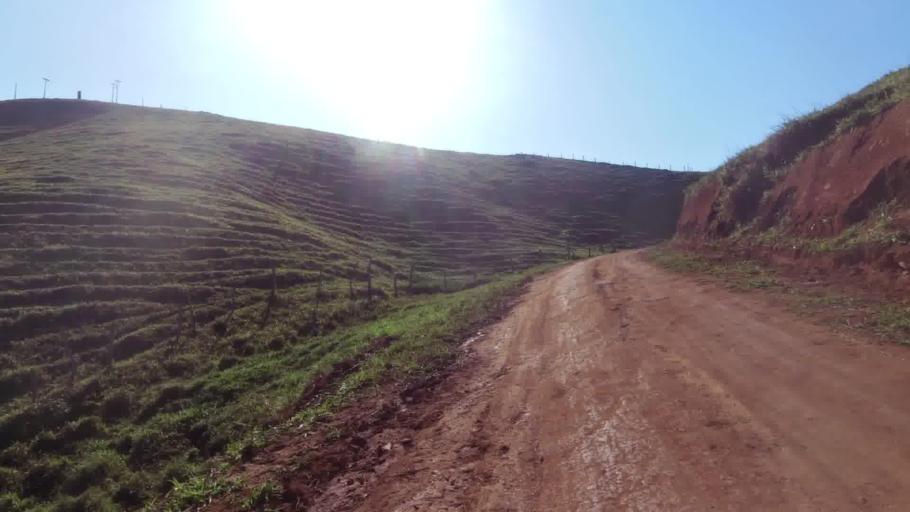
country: BR
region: Espirito Santo
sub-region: Alfredo Chaves
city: Alfredo Chaves
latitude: -20.6705
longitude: -40.7814
